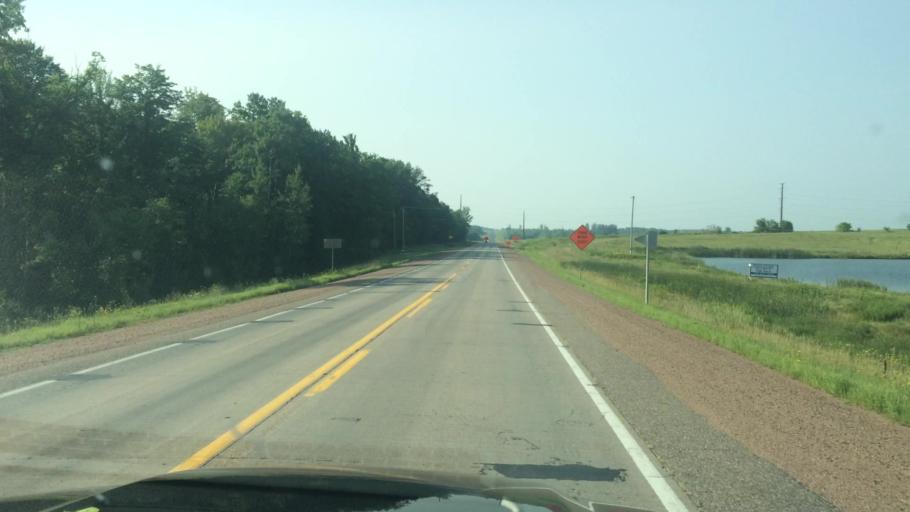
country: US
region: Wisconsin
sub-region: Marathon County
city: Athens
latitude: 44.9405
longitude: -90.0792
